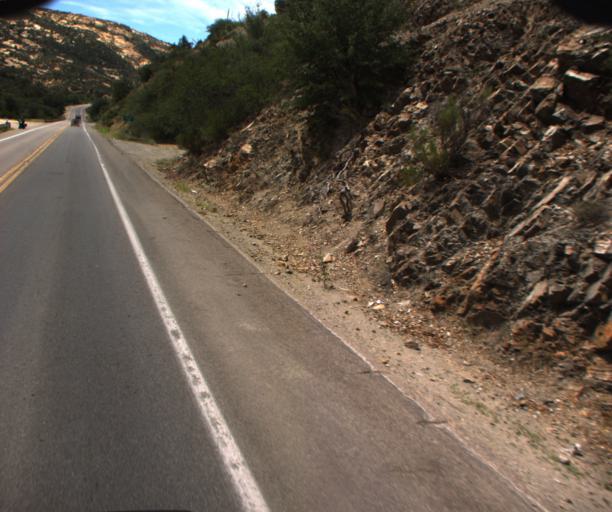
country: US
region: Arizona
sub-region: Gila County
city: Miami
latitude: 33.3868
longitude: -110.8883
